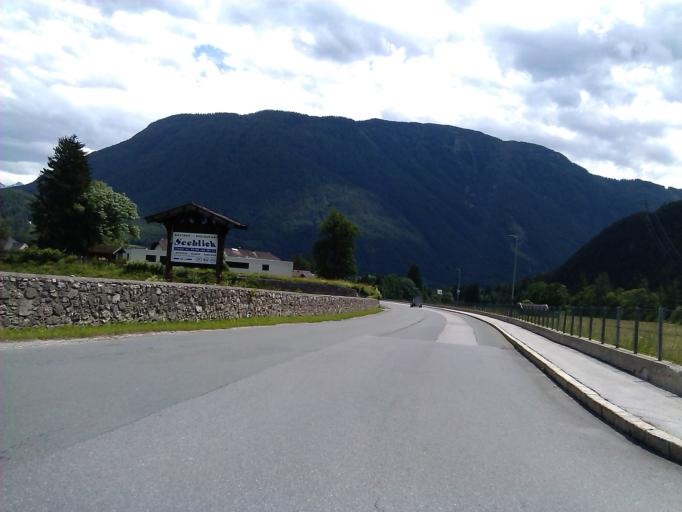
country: AT
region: Tyrol
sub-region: Politischer Bezirk Imst
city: Nassereith
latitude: 47.3173
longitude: 10.8327
